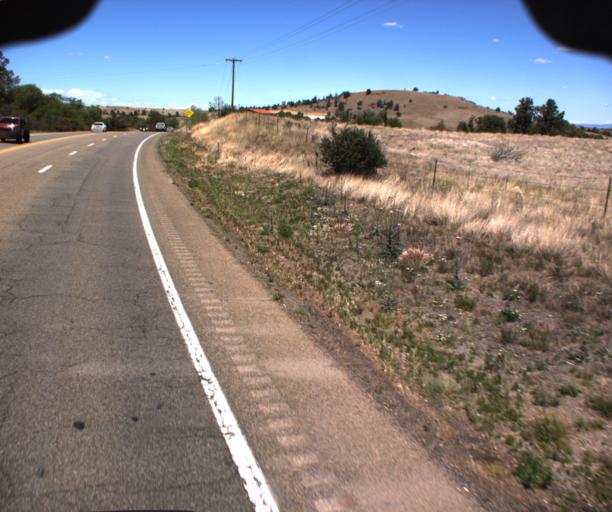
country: US
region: Arizona
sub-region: Yavapai County
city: Prescott
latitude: 34.6185
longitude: -112.4238
